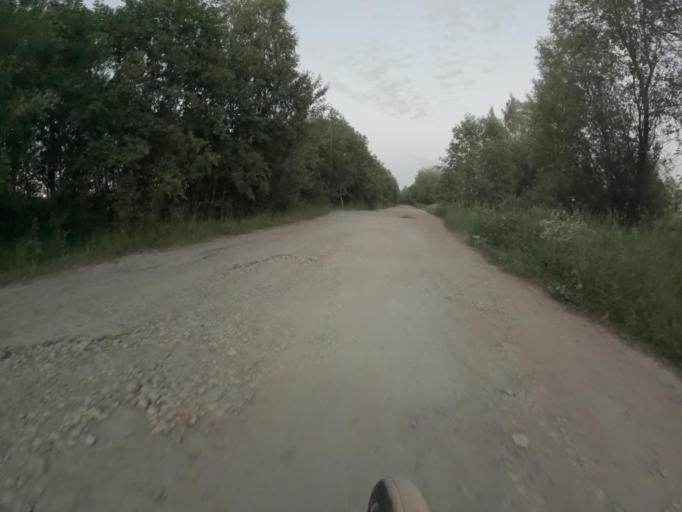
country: RU
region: St.-Petersburg
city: Sapernyy
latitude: 59.7804
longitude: 30.6650
